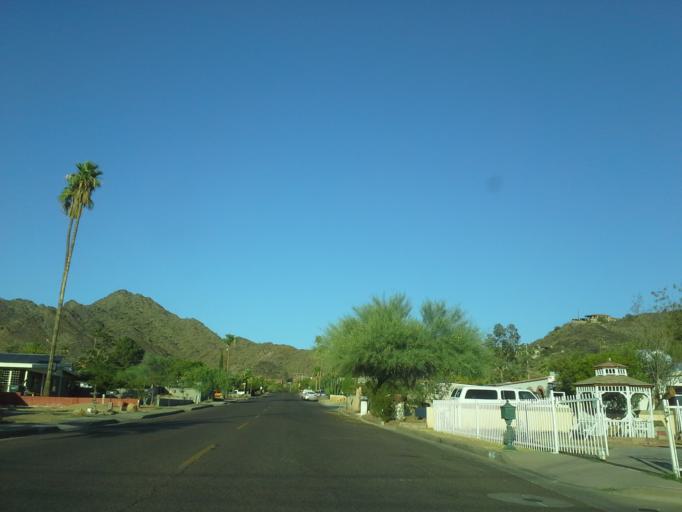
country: US
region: Arizona
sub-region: Maricopa County
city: Paradise Valley
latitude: 33.5713
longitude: -112.0511
